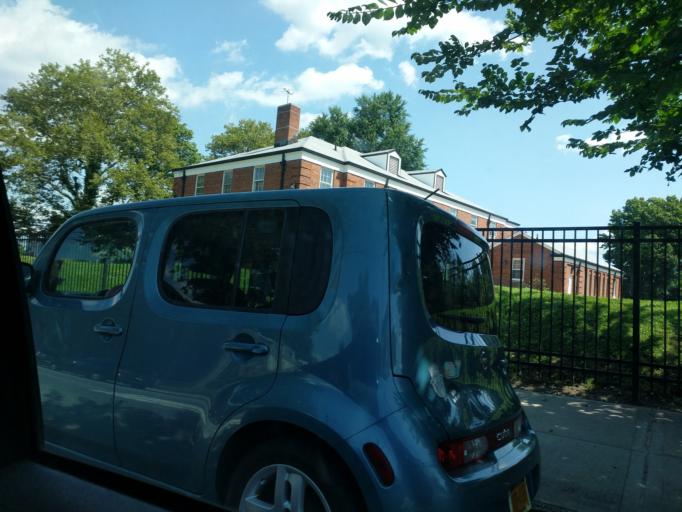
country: US
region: New Jersey
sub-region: Hudson County
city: Bayonne
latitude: 40.6342
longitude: -74.1144
